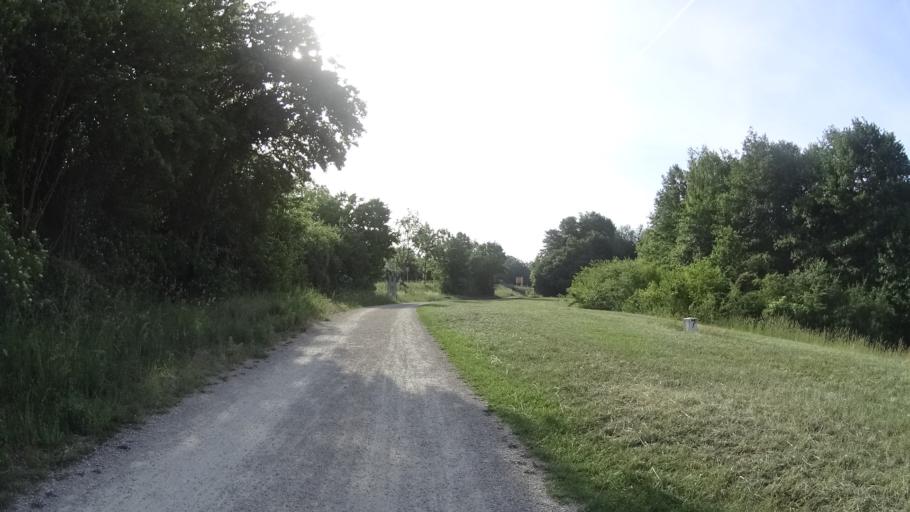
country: DE
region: Bavaria
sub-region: Lower Bavaria
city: Riedenburg
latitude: 48.9618
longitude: 11.6876
